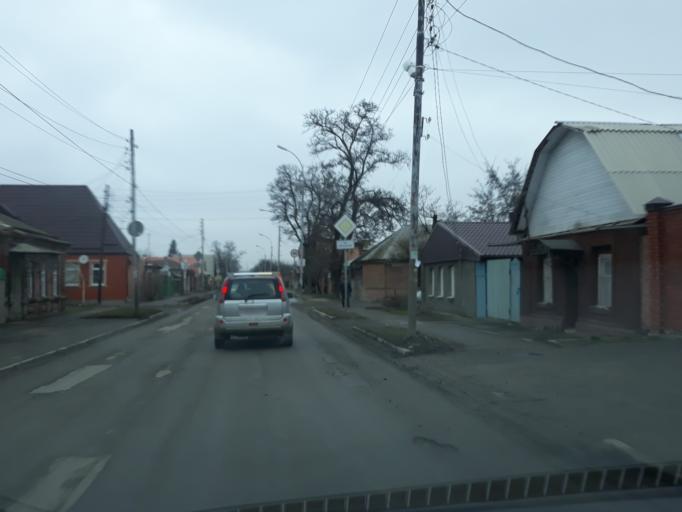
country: RU
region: Rostov
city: Taganrog
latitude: 47.2255
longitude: 38.9239
